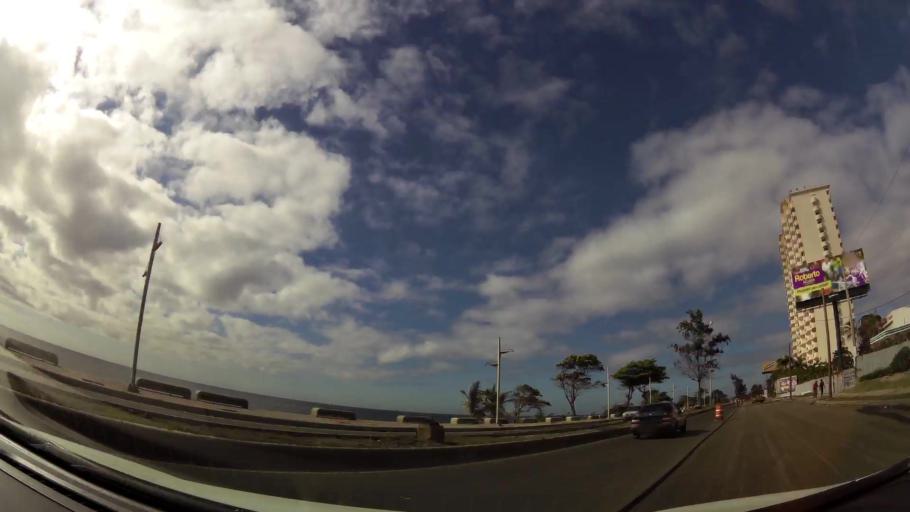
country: DO
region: Nacional
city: Bella Vista
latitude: 18.4427
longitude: -69.9282
